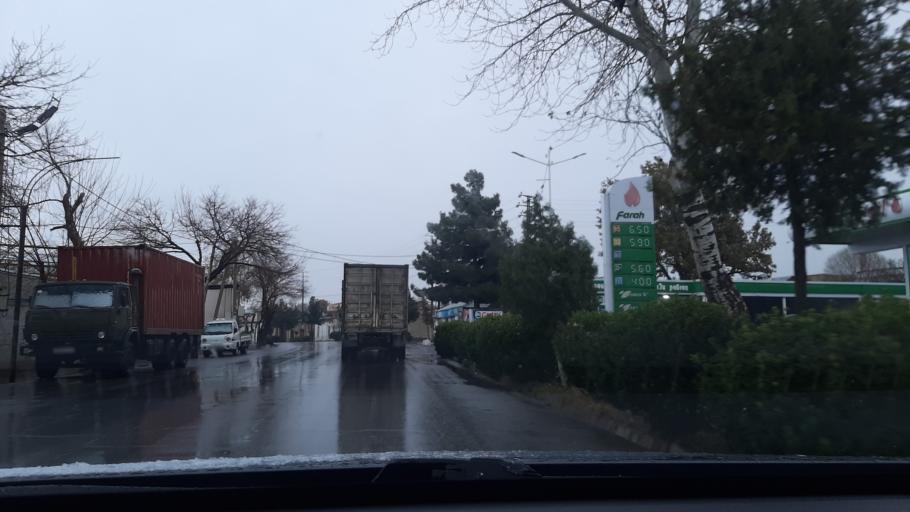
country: TJ
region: Viloyati Sughd
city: Khujand
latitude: 40.2708
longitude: 69.6359
